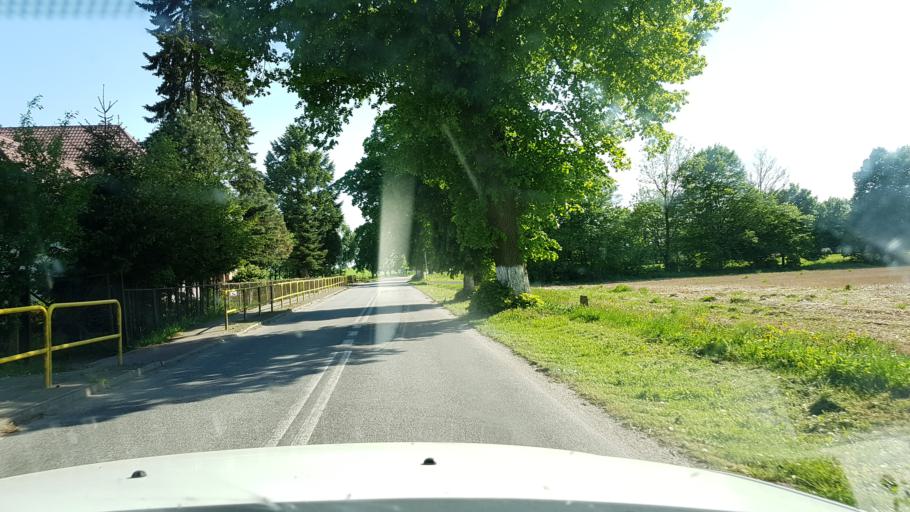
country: PL
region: West Pomeranian Voivodeship
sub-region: Powiat lobeski
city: Resko
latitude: 53.8093
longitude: 15.4197
